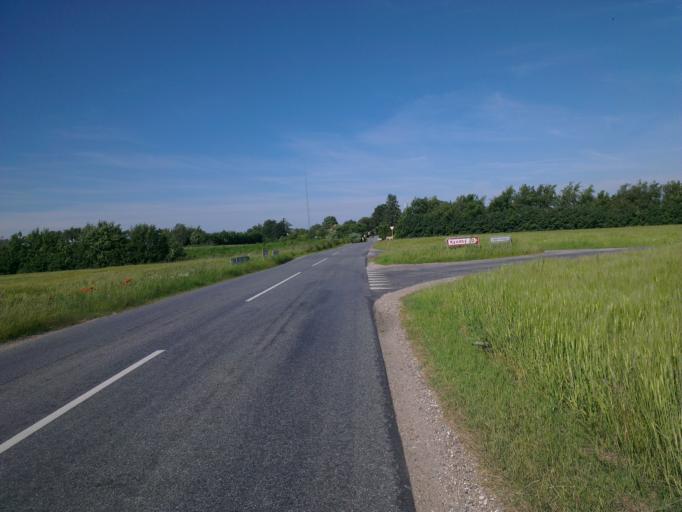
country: DK
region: Capital Region
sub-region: Frederikssund Kommune
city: Skibby
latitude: 55.7777
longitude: 11.9126
